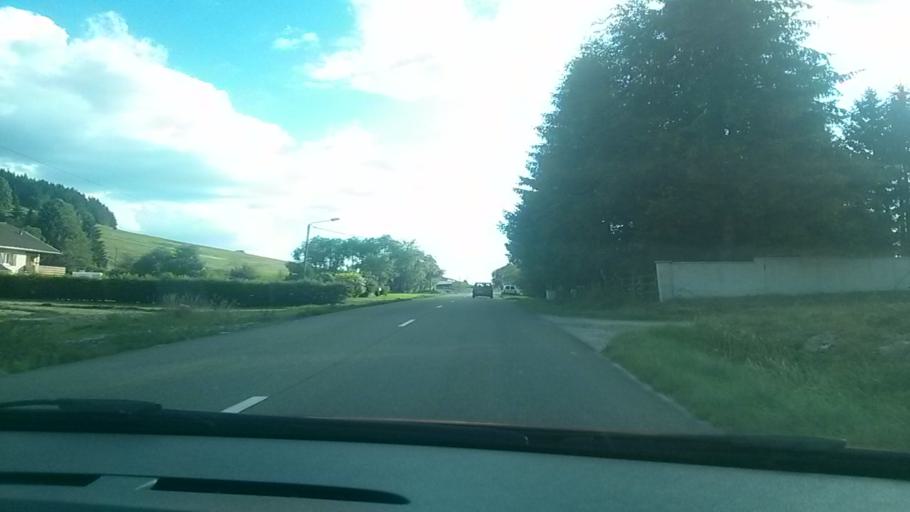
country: FR
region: Franche-Comte
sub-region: Departement du Jura
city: Les Rousses
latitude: 46.5142
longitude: 6.1150
